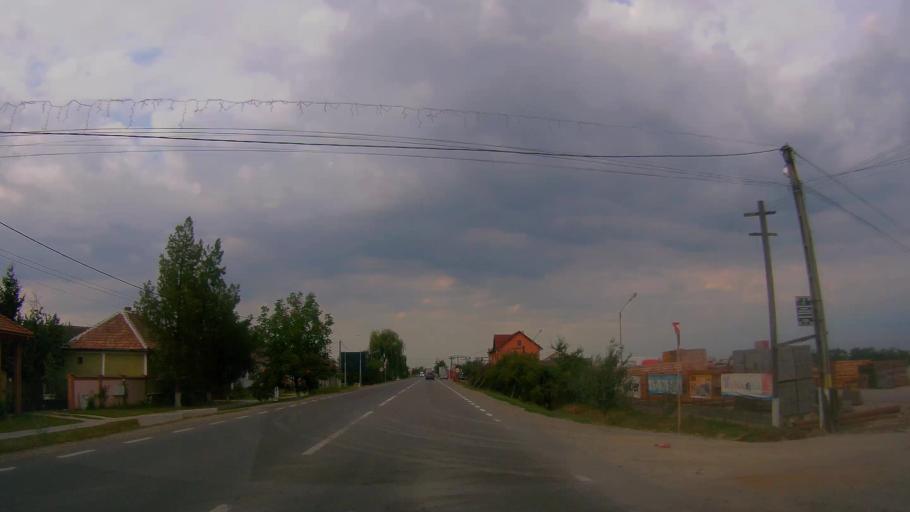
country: RO
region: Satu Mare
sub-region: Comuna Botiz
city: Botiz
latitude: 47.8247
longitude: 22.9446
